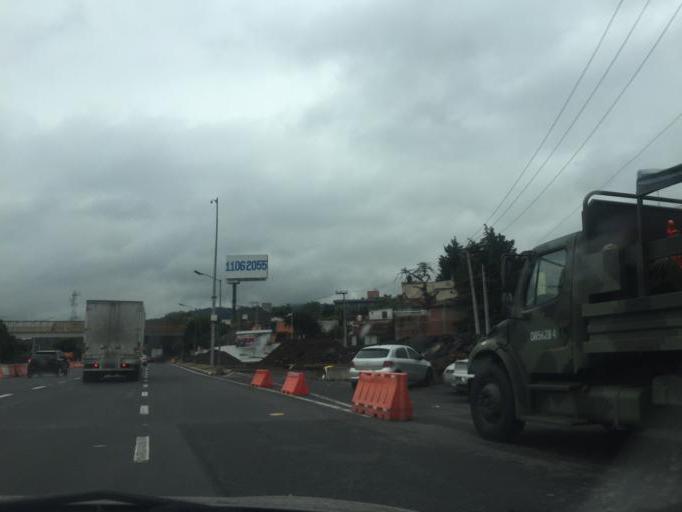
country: MX
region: Mexico City
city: Xochimilco
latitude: 19.2411
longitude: -99.1481
